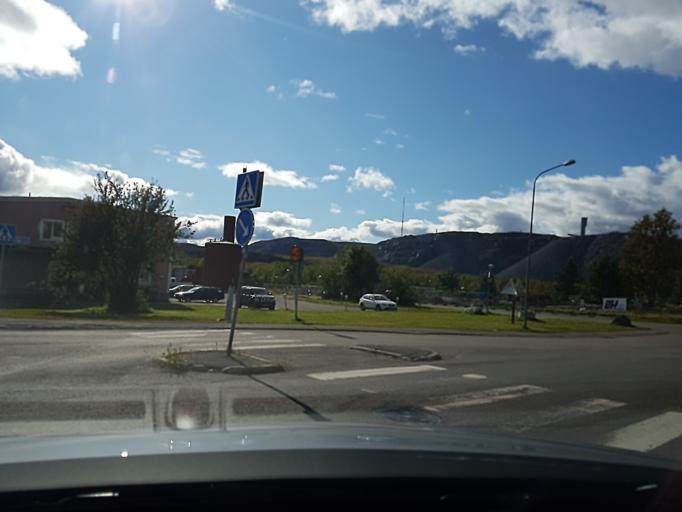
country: SE
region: Norrbotten
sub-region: Kiruna Kommun
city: Kiruna
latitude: 67.8459
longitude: 20.2308
